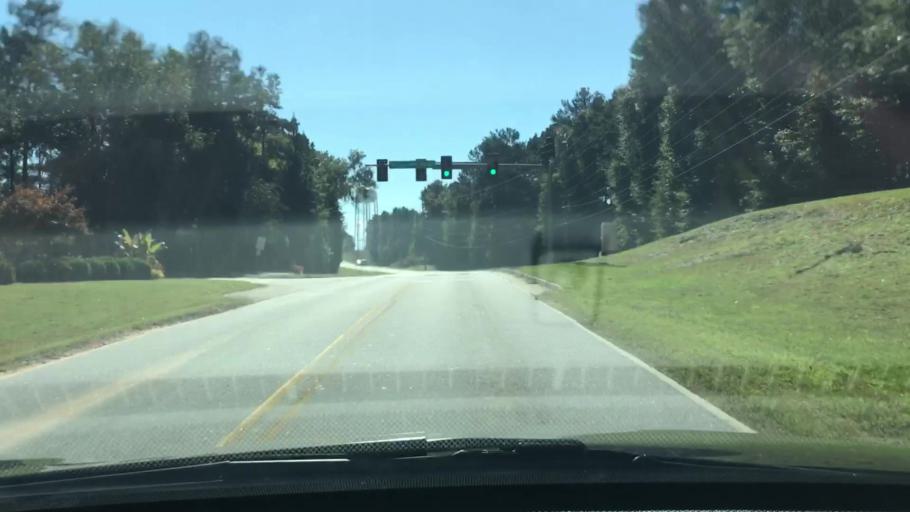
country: US
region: Georgia
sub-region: Carroll County
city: Villa Rica
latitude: 33.7379
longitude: -84.9053
